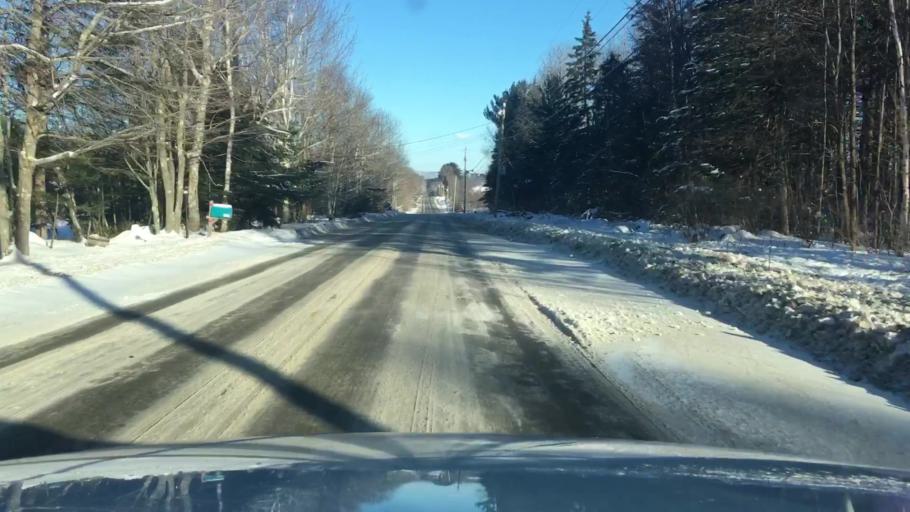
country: US
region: Maine
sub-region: Kennebec County
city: Mount Vernon
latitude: 44.4574
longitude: -69.9714
